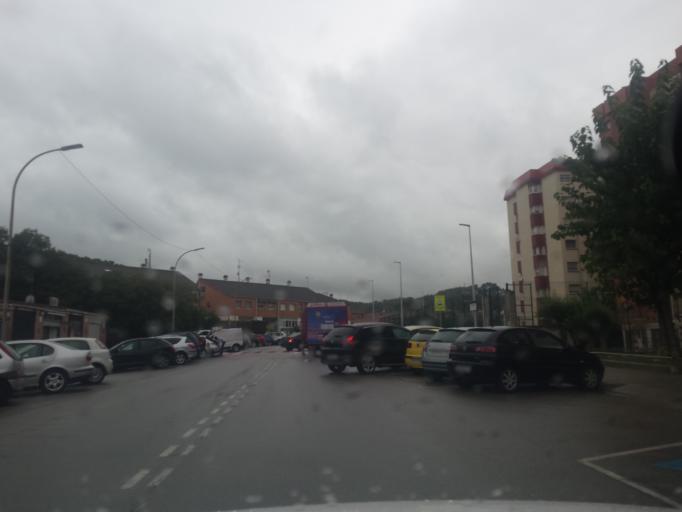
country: ES
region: Catalonia
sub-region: Provincia de Barcelona
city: Sant Andreu de la Barca
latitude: 41.4542
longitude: 1.9589
